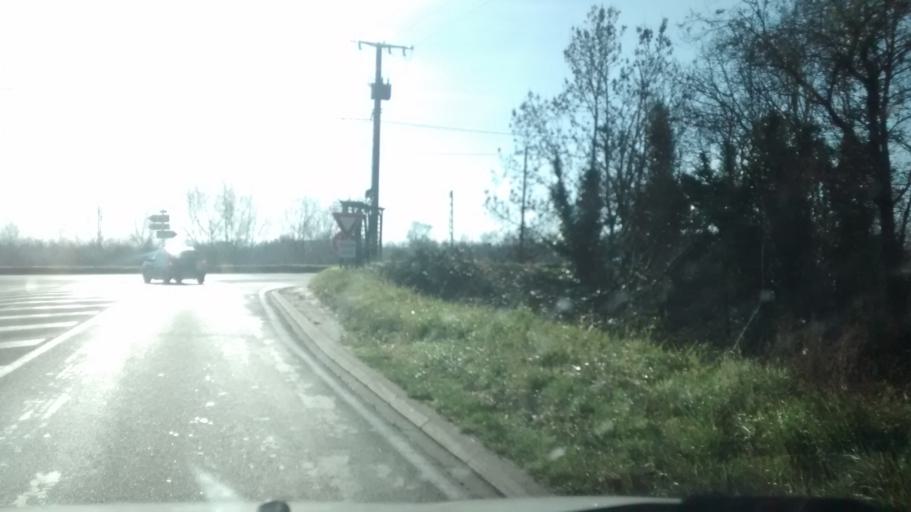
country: FR
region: Centre
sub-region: Departement d'Indre-et-Loire
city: Amboise
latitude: 47.4134
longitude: 0.9634
